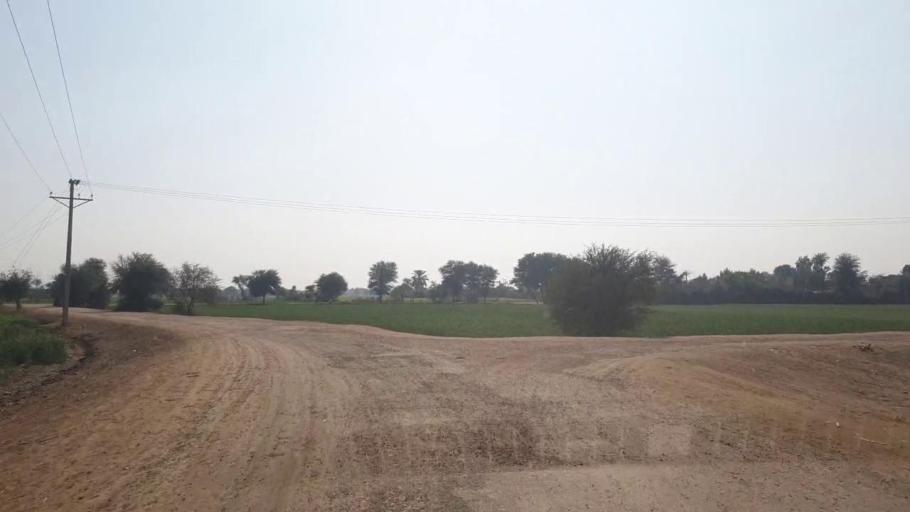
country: PK
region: Sindh
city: Shahdadpur
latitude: 26.0390
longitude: 68.4625
